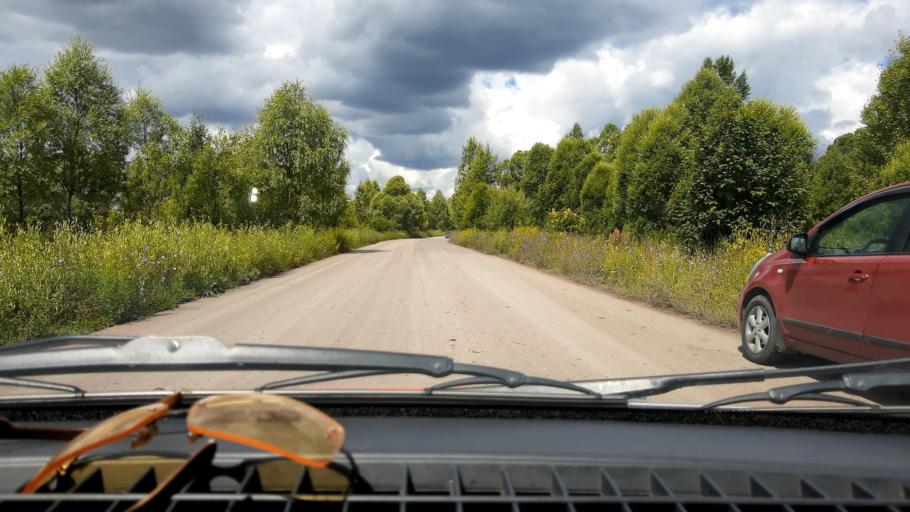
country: RU
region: Bashkortostan
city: Ufa
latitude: 54.7011
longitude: 56.1243
